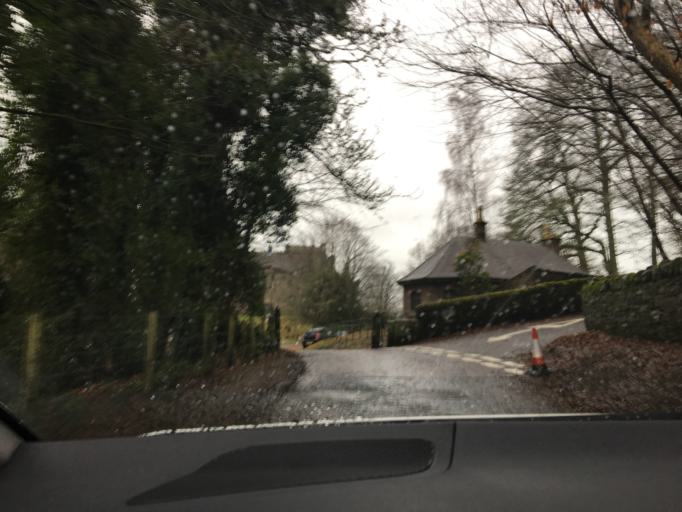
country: GB
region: Scotland
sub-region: Stirling
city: Doune
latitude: 56.1866
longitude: -4.0500
